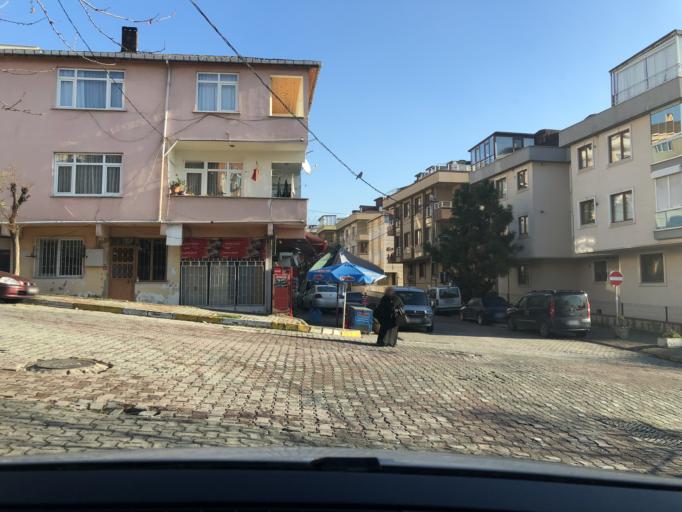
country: TR
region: Istanbul
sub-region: Atasehir
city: Atasehir
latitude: 40.9753
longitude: 29.1247
